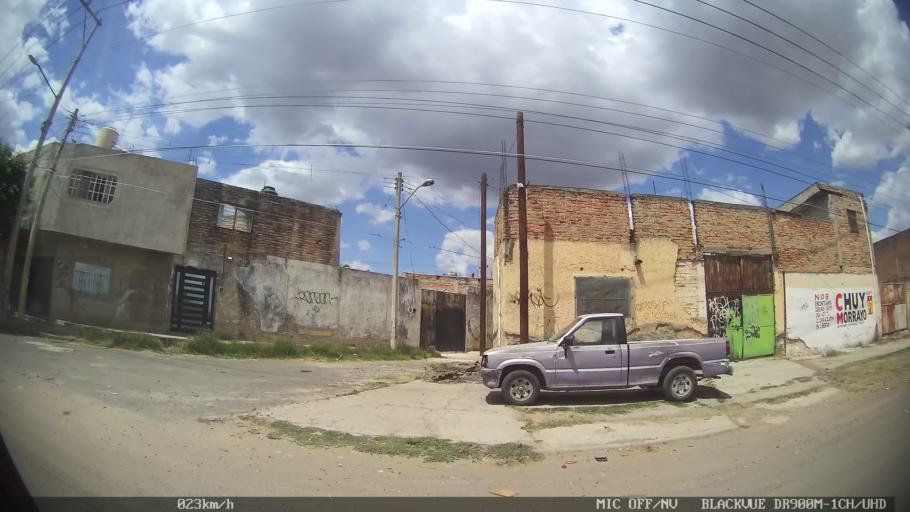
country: MX
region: Jalisco
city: Tlaquepaque
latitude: 20.6770
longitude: -103.2657
